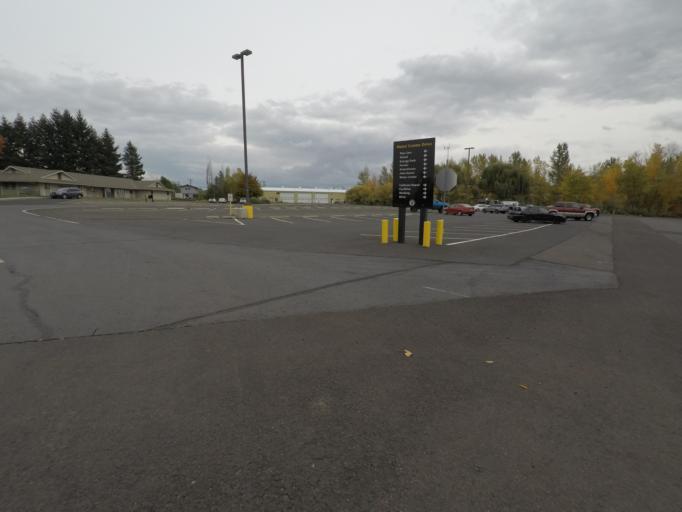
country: US
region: Washington
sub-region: Walla Walla County
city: Walla Walla East
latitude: 46.0800
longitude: -118.2750
